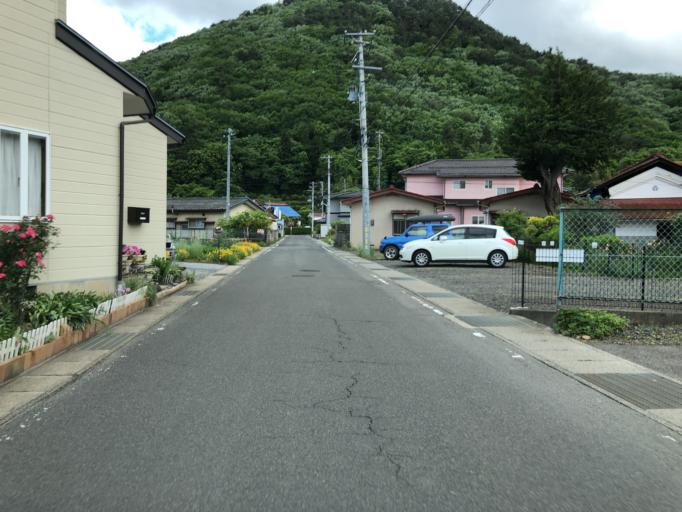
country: JP
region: Fukushima
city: Fukushima-shi
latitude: 37.7751
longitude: 140.4595
